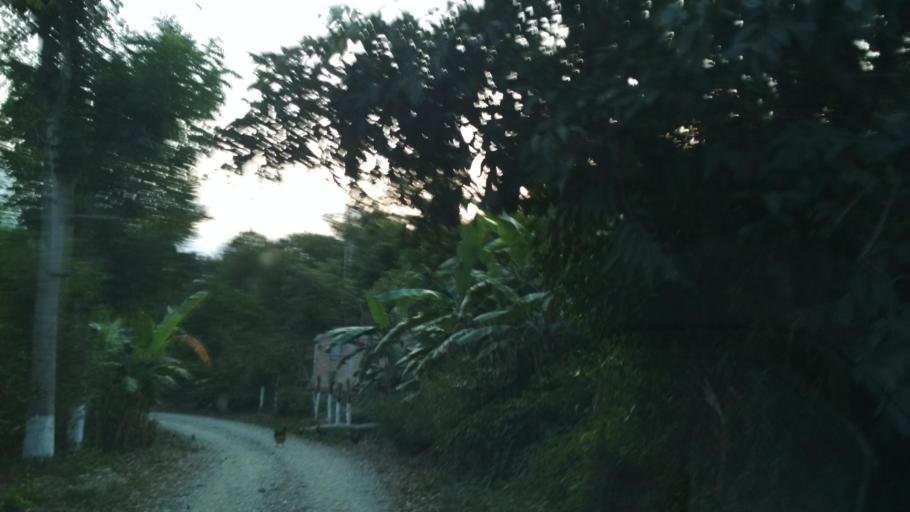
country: MX
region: Veracruz
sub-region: Poza Rica de Hidalgo
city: Arroyo del Maiz Uno
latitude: 20.4755
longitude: -97.3927
